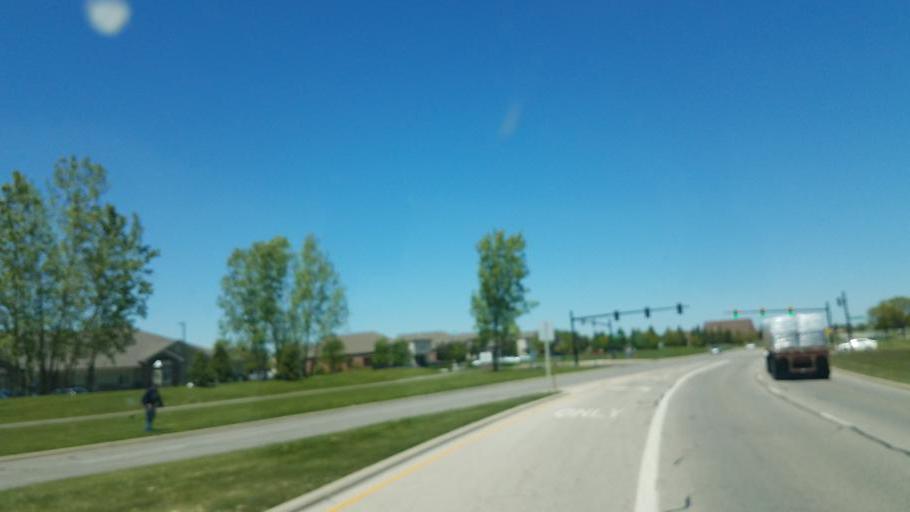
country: US
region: Ohio
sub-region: Delaware County
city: Powell
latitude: 40.1472
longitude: -83.0932
